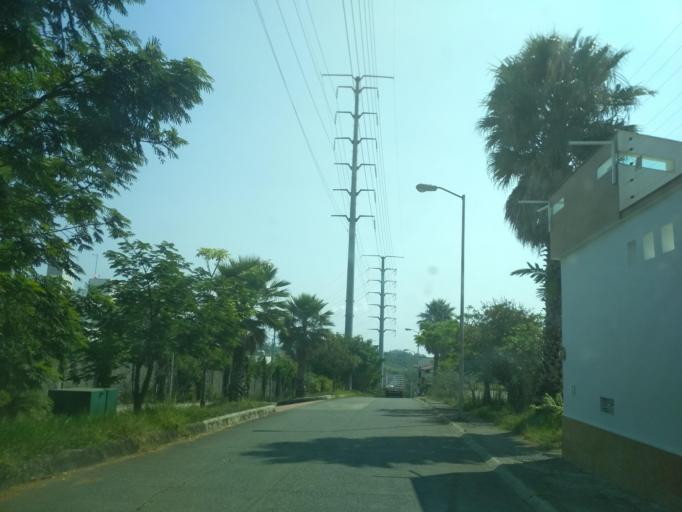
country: MX
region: Veracruz
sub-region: Emiliano Zapata
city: Las Trancas
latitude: 19.5239
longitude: -96.8662
